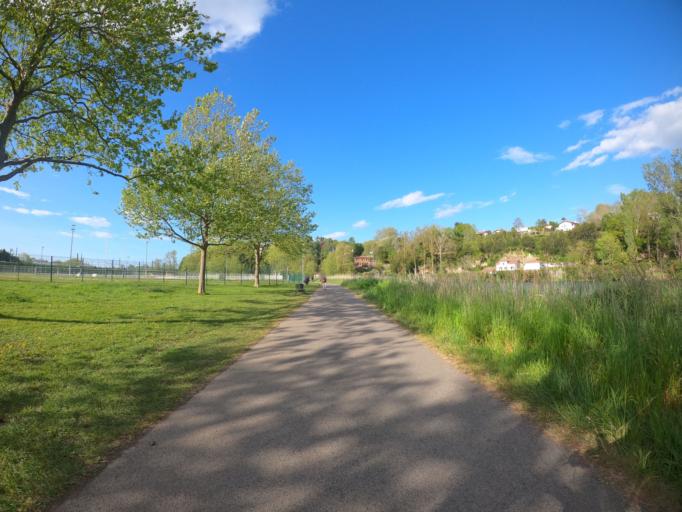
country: FR
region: Aquitaine
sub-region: Departement des Pyrenees-Atlantiques
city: Bayonne
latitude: 43.4799
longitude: -1.4711
